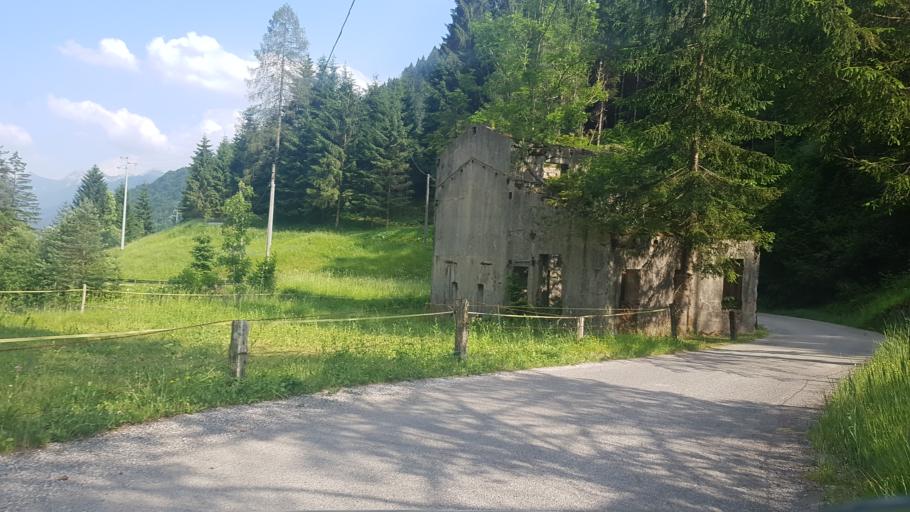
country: IT
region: Friuli Venezia Giulia
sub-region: Provincia di Udine
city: Pontebba
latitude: 46.5240
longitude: 13.2606
